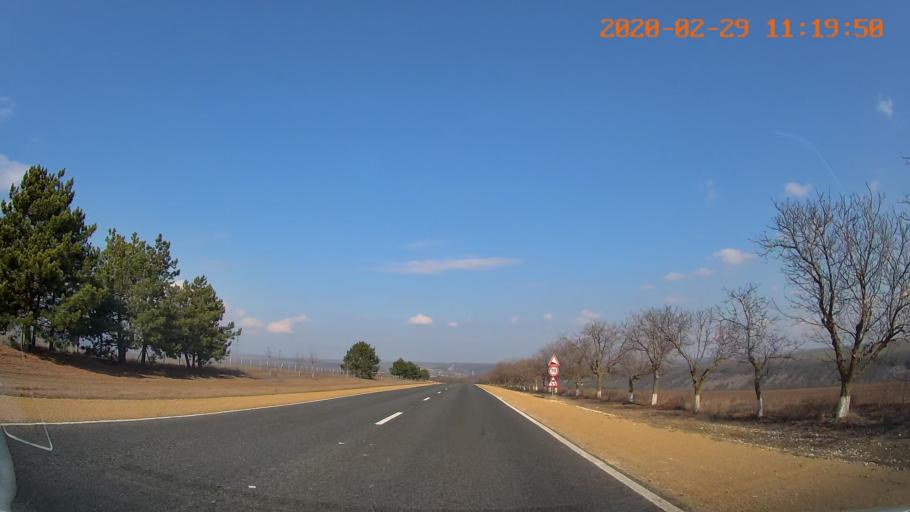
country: MD
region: Telenesti
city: Cocieri
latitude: 47.3561
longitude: 29.1732
